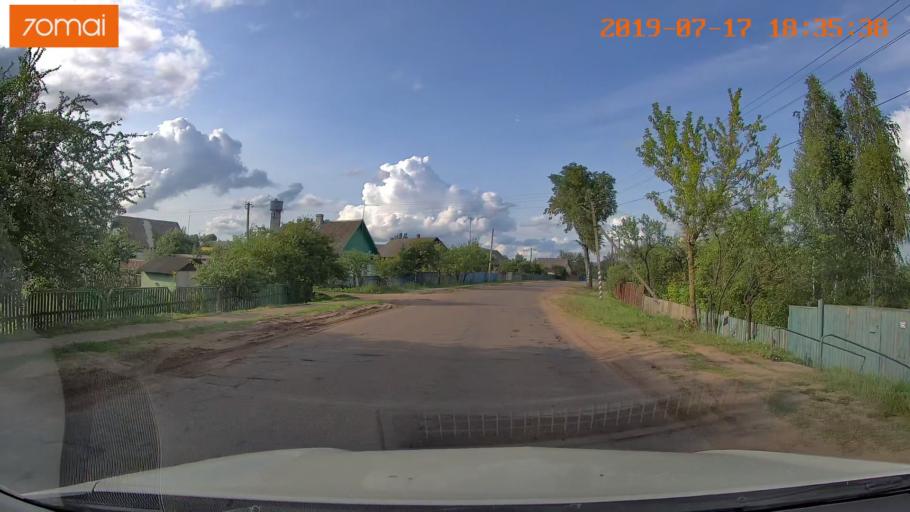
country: BY
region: Mogilev
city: Asipovichy
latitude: 53.2938
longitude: 28.6588
